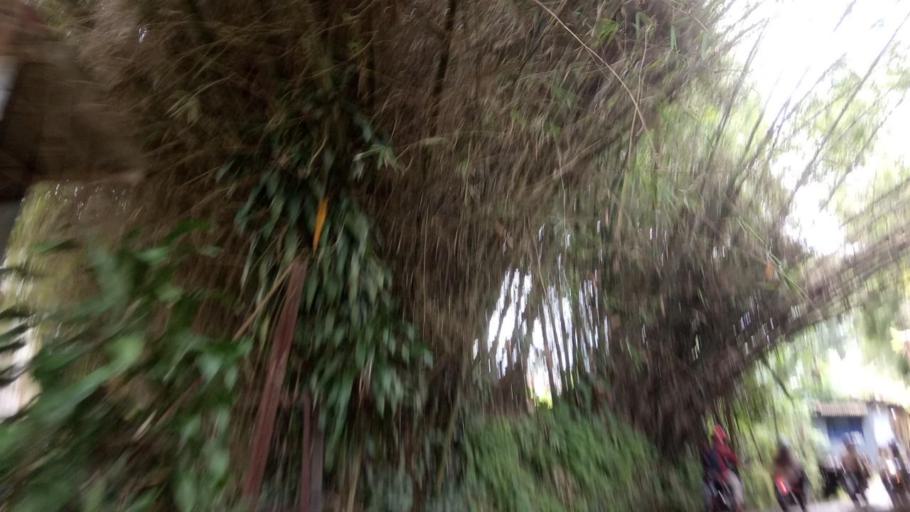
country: ID
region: West Java
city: Caringin
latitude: -6.6492
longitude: 106.8977
